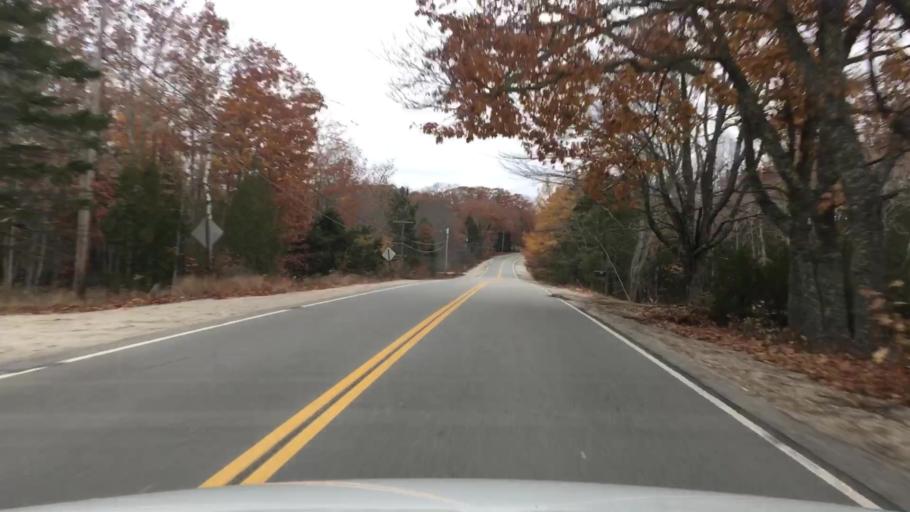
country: US
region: Maine
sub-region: Hancock County
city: Sedgwick
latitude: 44.3919
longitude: -68.5820
